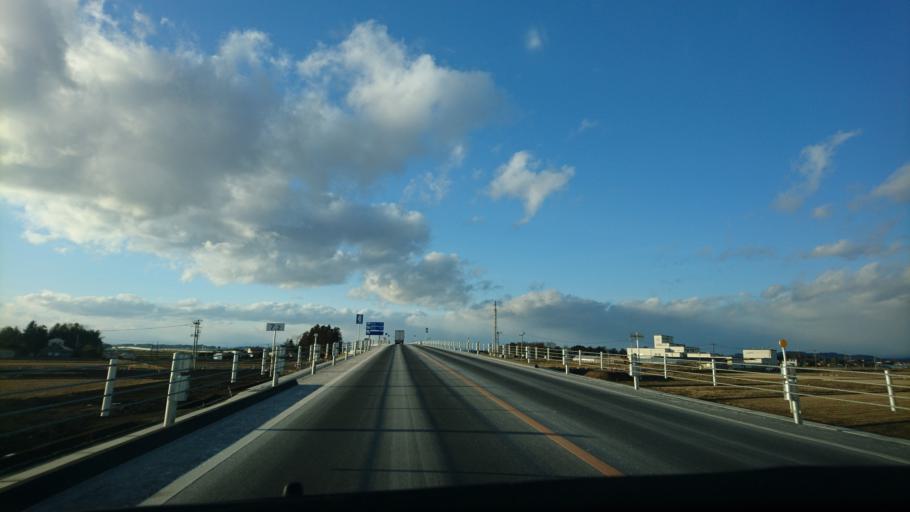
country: JP
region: Miyagi
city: Wakuya
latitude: 38.6823
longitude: 141.2525
